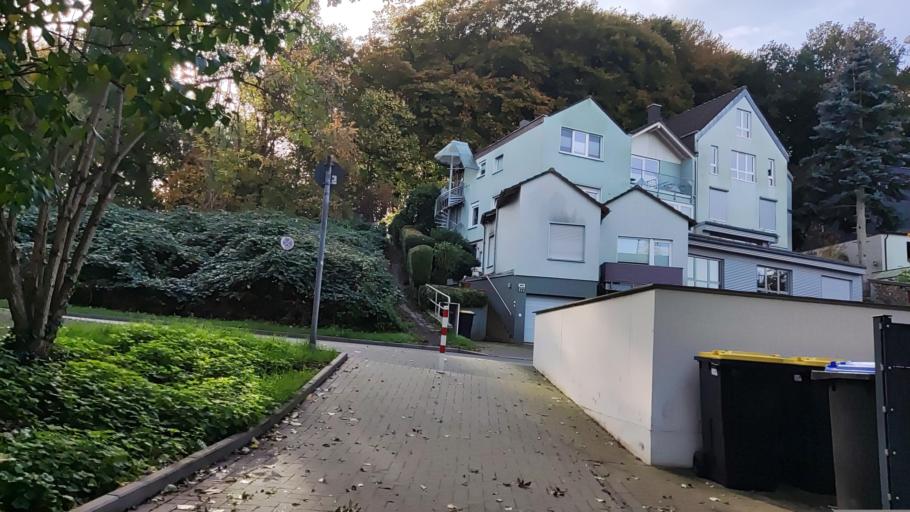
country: DE
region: North Rhine-Westphalia
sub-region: Regierungsbezirk Arnsberg
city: Herne
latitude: 51.5201
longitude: 7.2316
